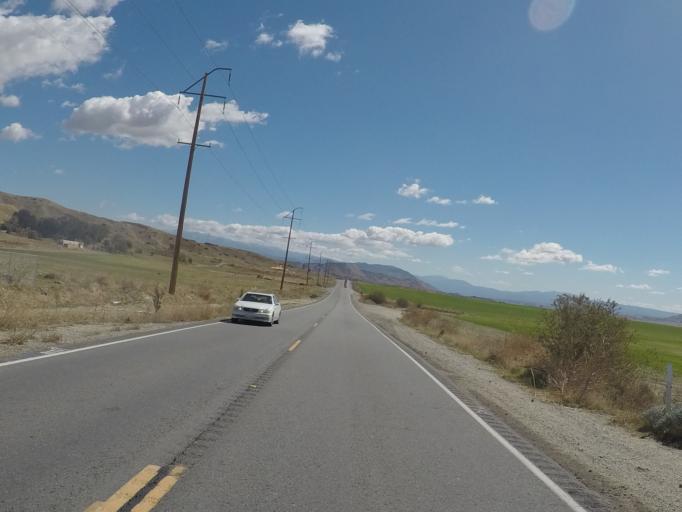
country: US
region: California
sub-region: Riverside County
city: Lakeview
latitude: 33.9264
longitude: -117.1176
